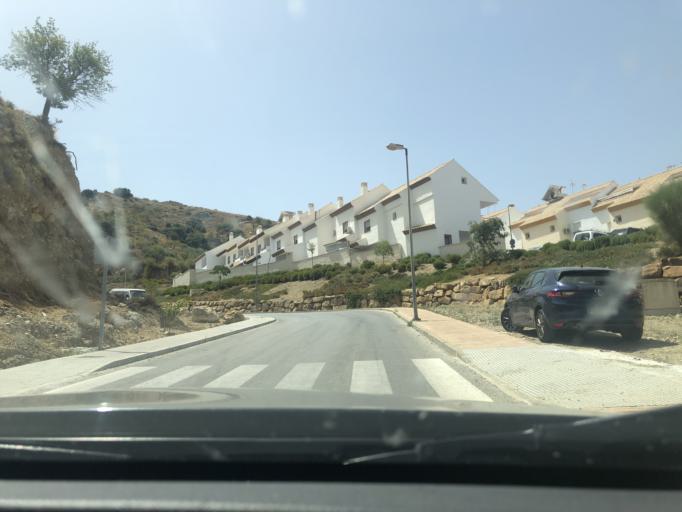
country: ES
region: Andalusia
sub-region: Provincia de Malaga
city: Cartama
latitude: 36.7119
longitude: -4.6253
